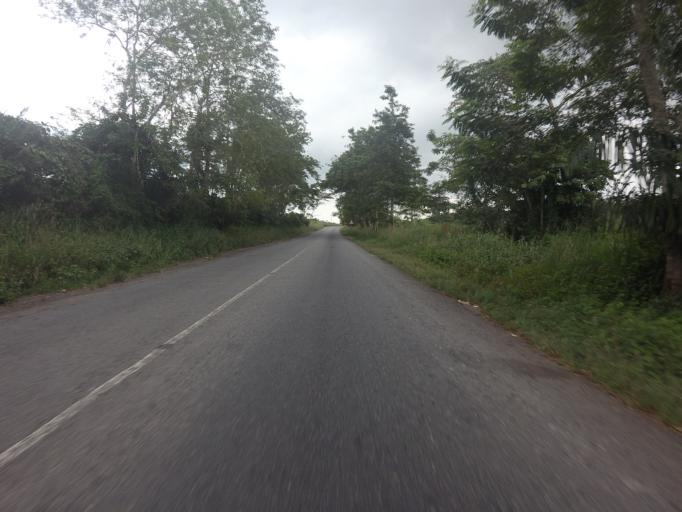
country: GH
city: Akropong
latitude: 5.9530
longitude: -0.1175
